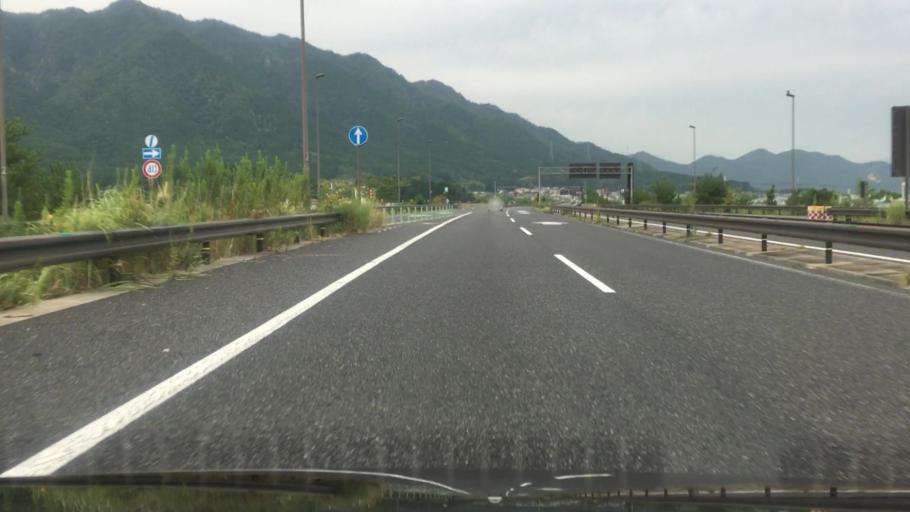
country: JP
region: Kyoto
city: Fukuchiyama
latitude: 35.1638
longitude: 135.1120
